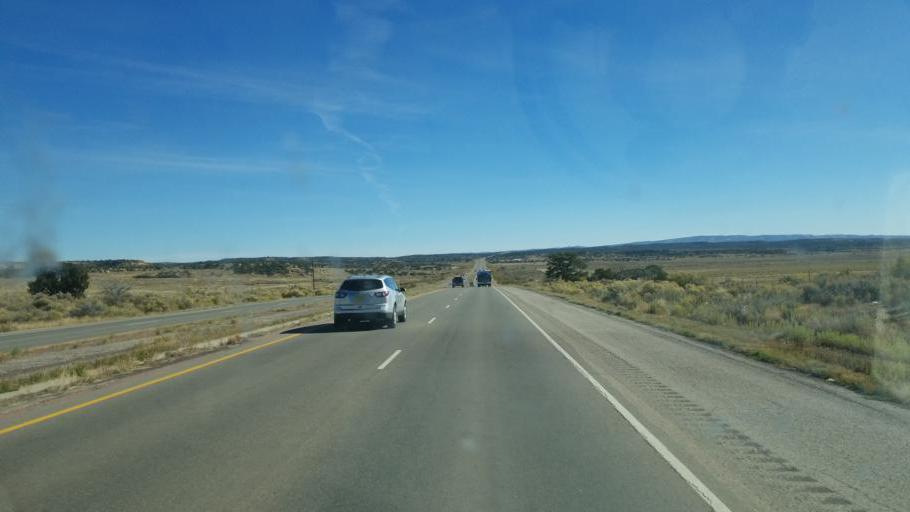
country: US
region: Arizona
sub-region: Apache County
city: Window Rock
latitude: 35.6270
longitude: -108.9357
